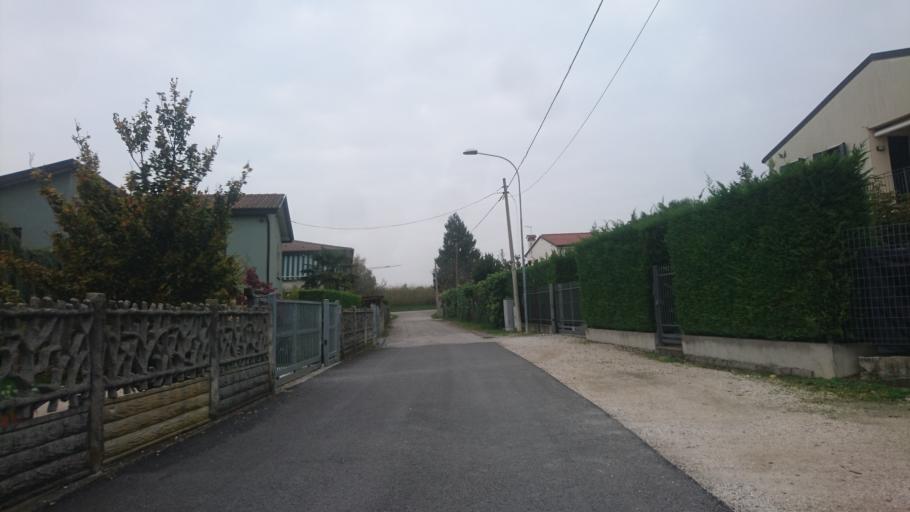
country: IT
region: Veneto
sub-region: Provincia di Padova
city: Oltre Brenta
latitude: 45.4070
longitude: 11.9921
